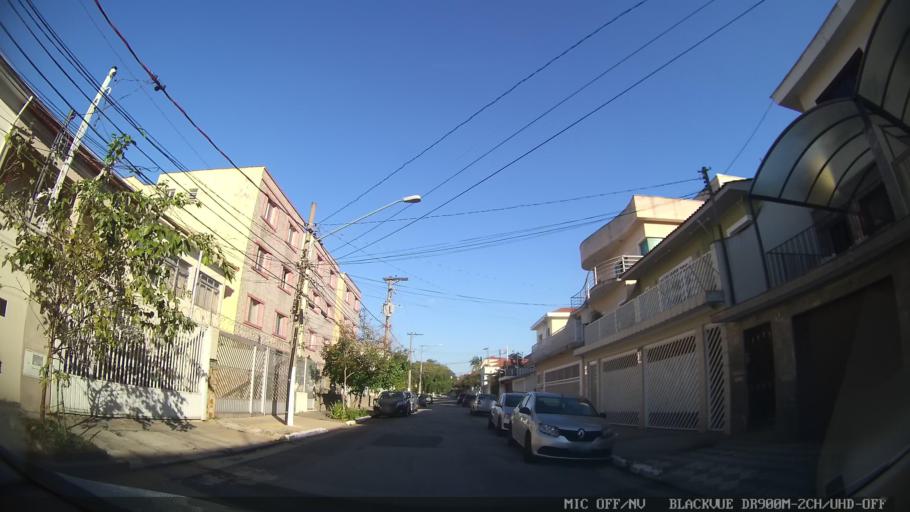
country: BR
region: Sao Paulo
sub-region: Sao Paulo
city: Sao Paulo
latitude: -23.4940
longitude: -46.6175
